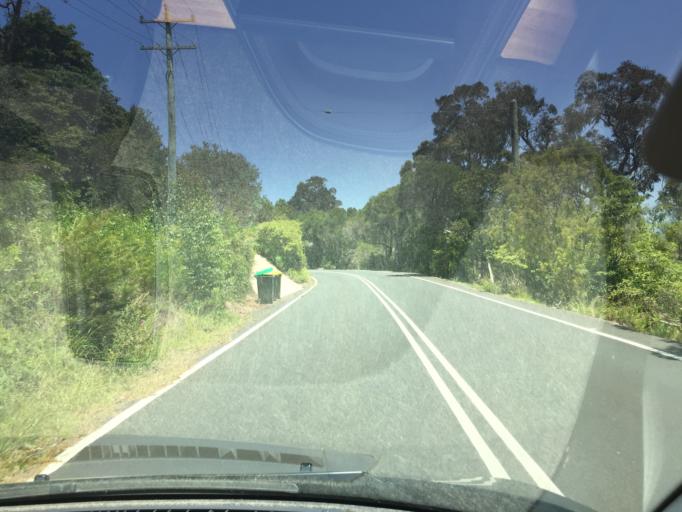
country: AU
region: New South Wales
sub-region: Bega Valley
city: Merimbula
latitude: -36.8905
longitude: 149.9243
